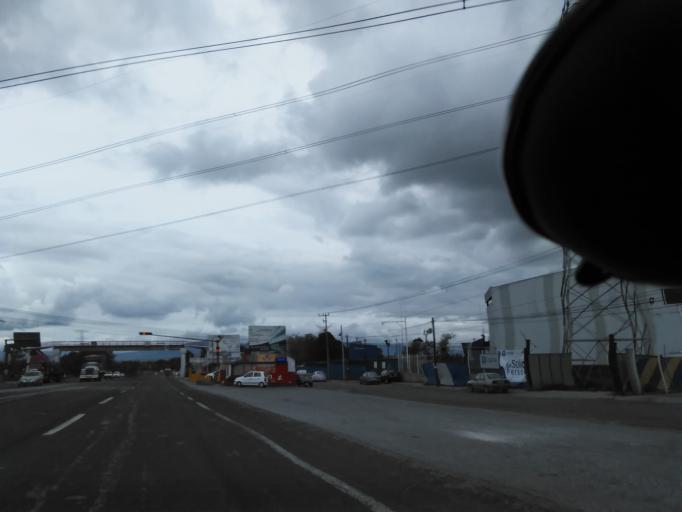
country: MX
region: Hidalgo
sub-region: Atitalaquia
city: Unidad Habitacional Antonio Osorio de Leon (Bojay)
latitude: 20.0561
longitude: -99.2676
